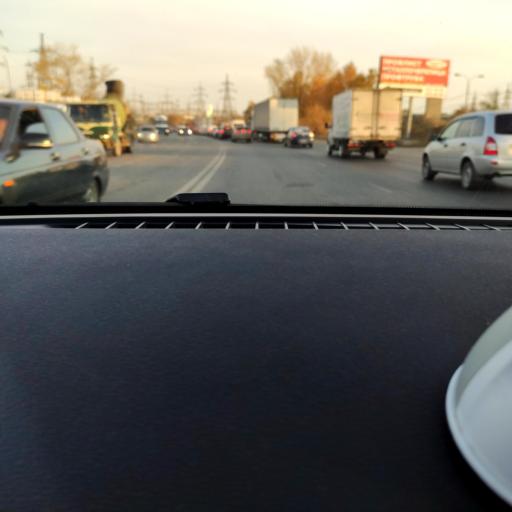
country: RU
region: Samara
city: Petra-Dubrava
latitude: 53.2594
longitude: 50.2919
